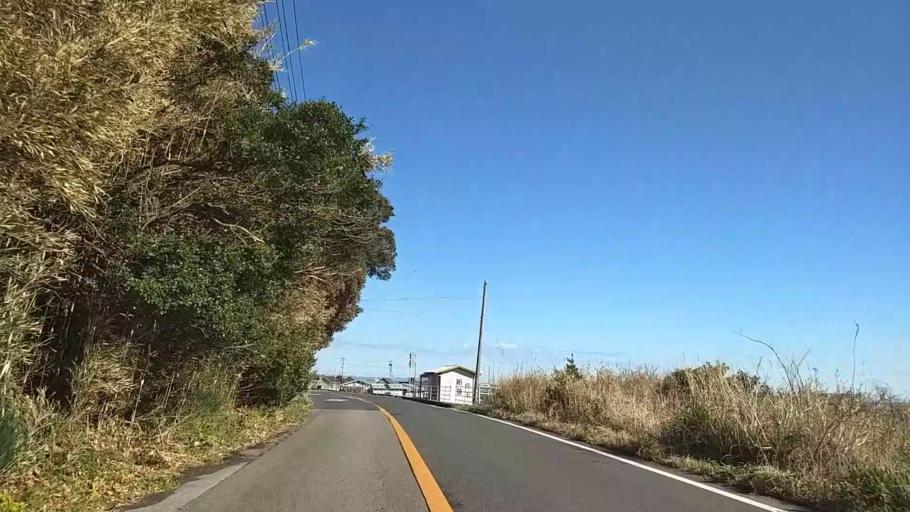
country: JP
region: Chiba
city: Tateyama
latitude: 34.9176
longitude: 139.9350
